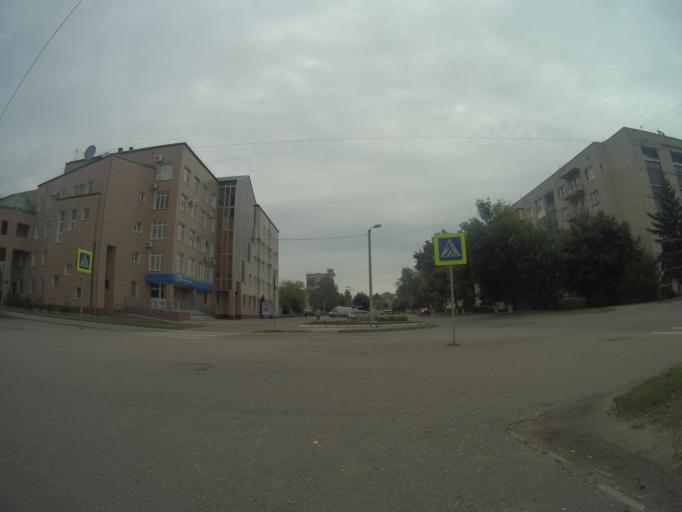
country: RU
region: Vladimir
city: Vladimir
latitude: 56.1186
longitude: 40.3719
